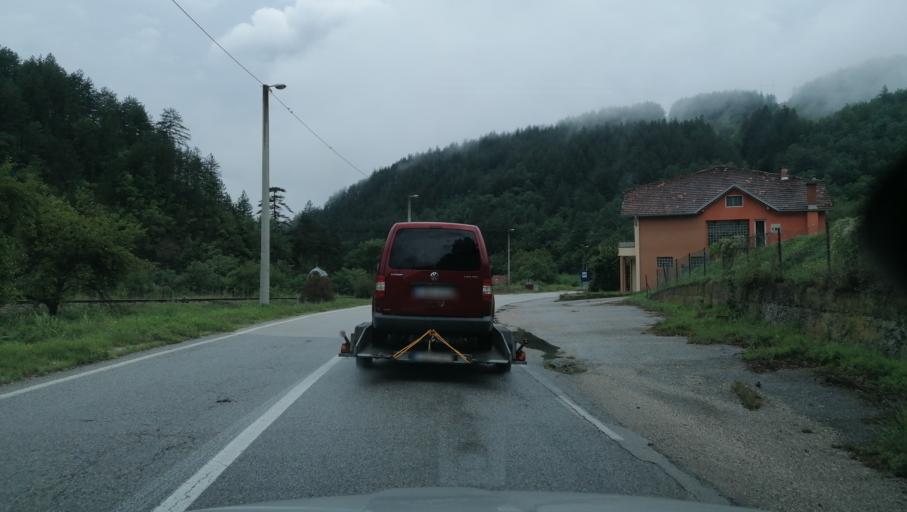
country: BA
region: Republika Srpska
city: Visegrad
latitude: 43.7821
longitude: 19.3577
